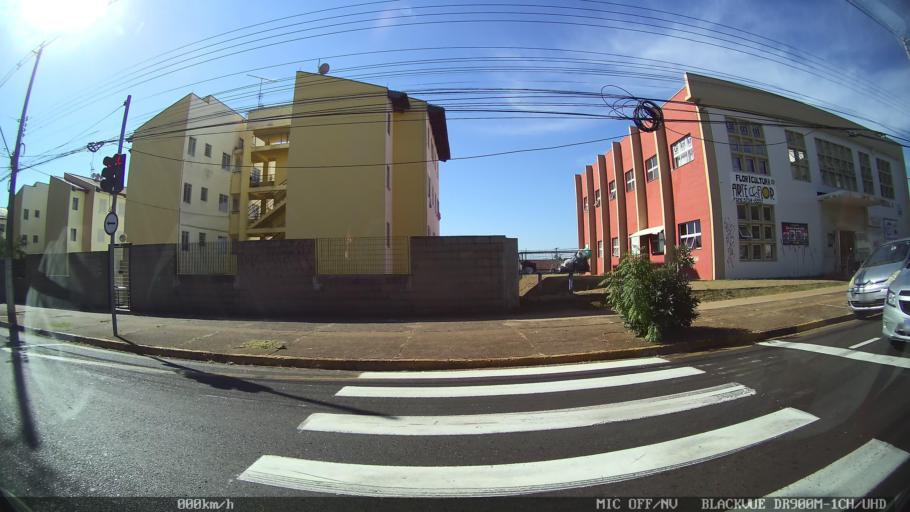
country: BR
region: Sao Paulo
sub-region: Franca
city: Franca
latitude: -20.5003
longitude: -47.4134
